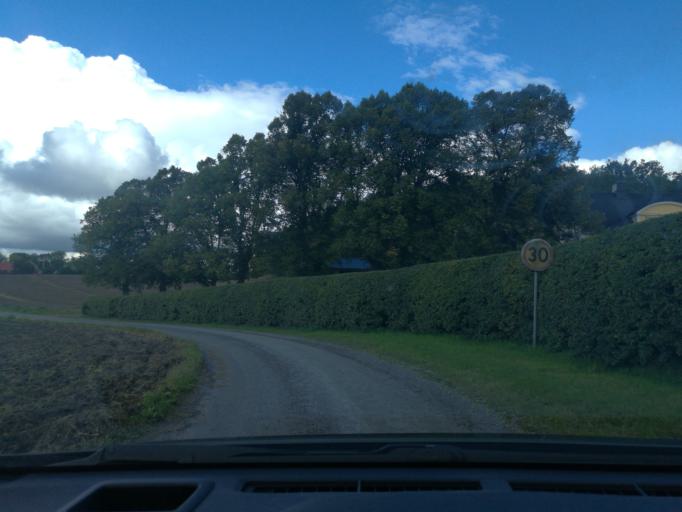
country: SE
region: OEstergoetland
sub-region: Soderkopings Kommun
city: Soederkoeping
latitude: 58.4929
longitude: 16.4754
